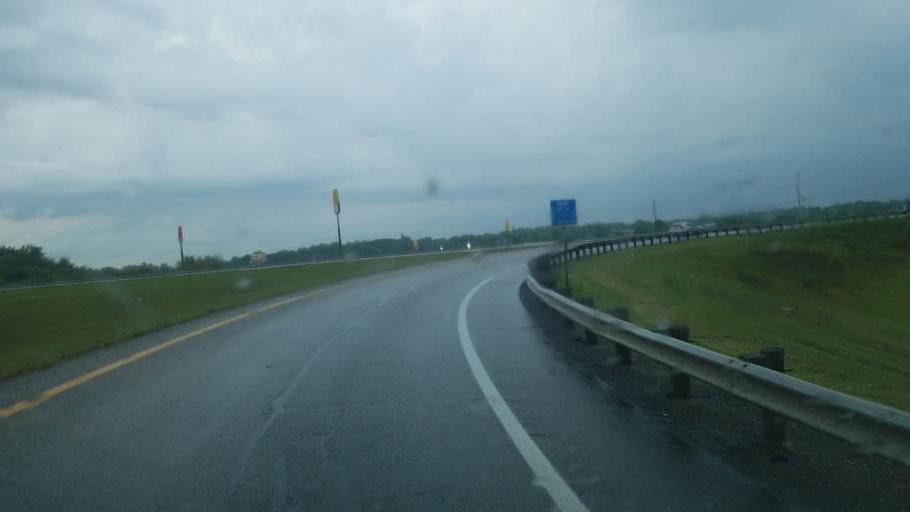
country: US
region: Ohio
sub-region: Trumbull County
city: Champion Heights
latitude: 41.2752
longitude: -80.8433
